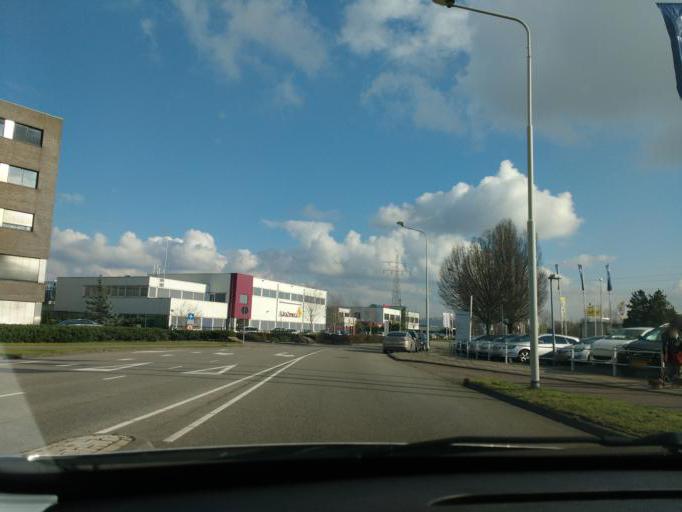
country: NL
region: Gelderland
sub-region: Gemeente Nijmegen
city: Lindenholt
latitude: 51.8414
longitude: 5.8055
